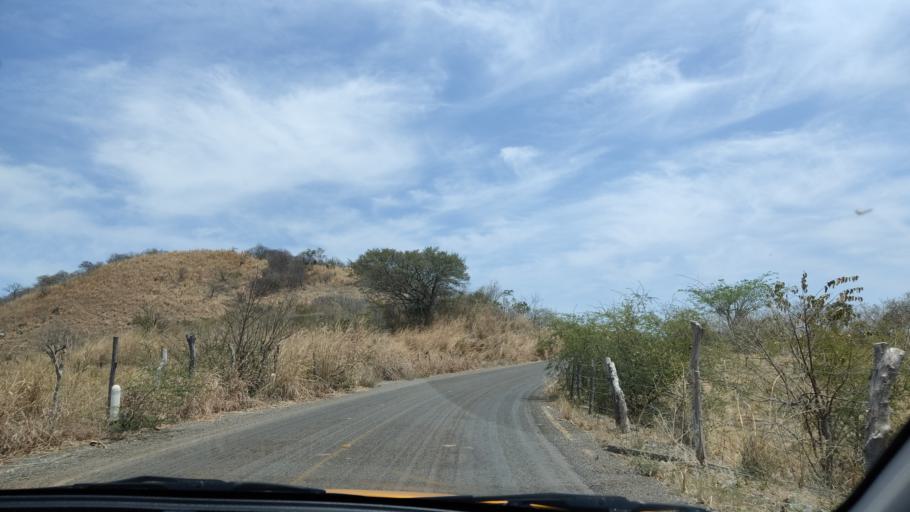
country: MX
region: Nayarit
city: Santa Maria del Oro
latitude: 21.5088
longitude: -104.6081
